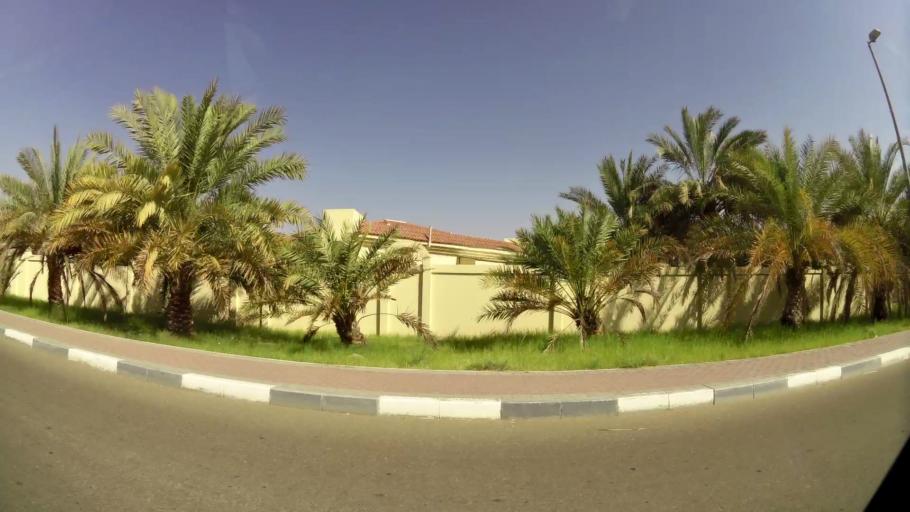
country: OM
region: Al Buraimi
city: Al Buraymi
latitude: 24.3318
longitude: 55.7961
